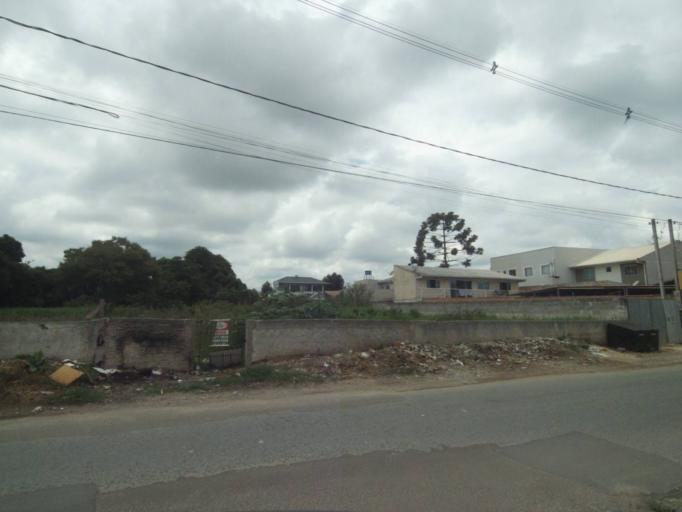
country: BR
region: Parana
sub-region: Pinhais
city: Pinhais
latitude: -25.4611
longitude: -49.1931
